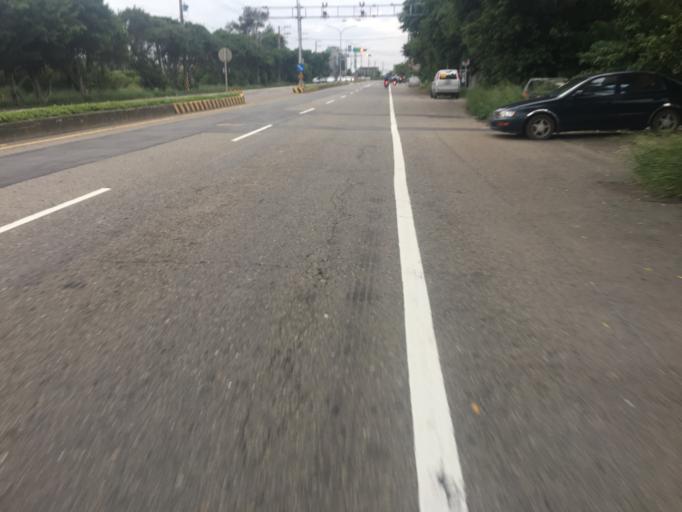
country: TW
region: Taiwan
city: Taoyuan City
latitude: 25.0917
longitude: 121.2308
